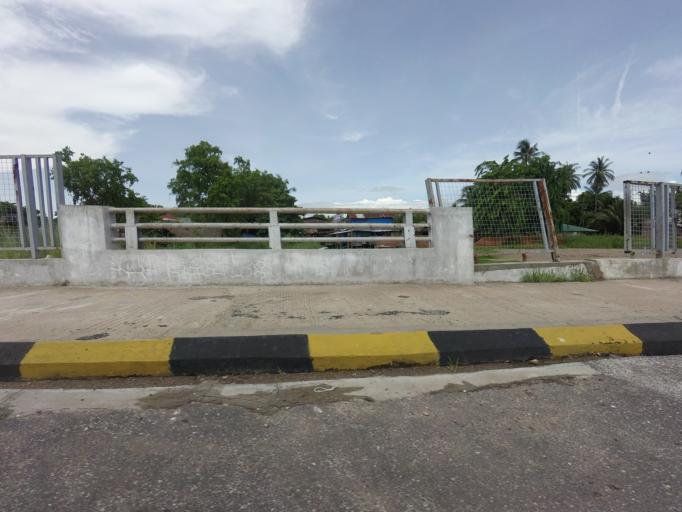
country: MM
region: Mon
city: Mawlamyine
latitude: 16.4617
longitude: 97.6229
